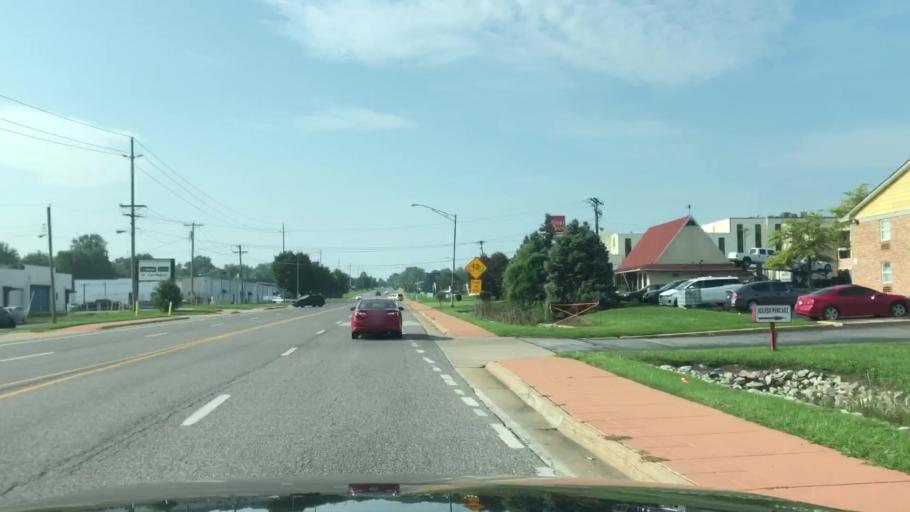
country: US
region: Missouri
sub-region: Saint Louis County
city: Woodson Terrace
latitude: 38.7348
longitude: -90.3569
